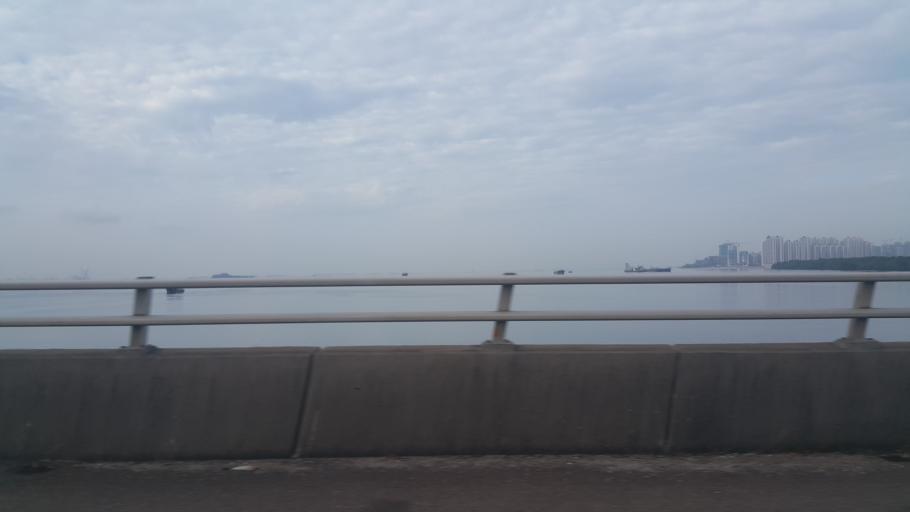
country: MY
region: Johor
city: Johor Bahru
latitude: 1.3572
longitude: 103.6245
